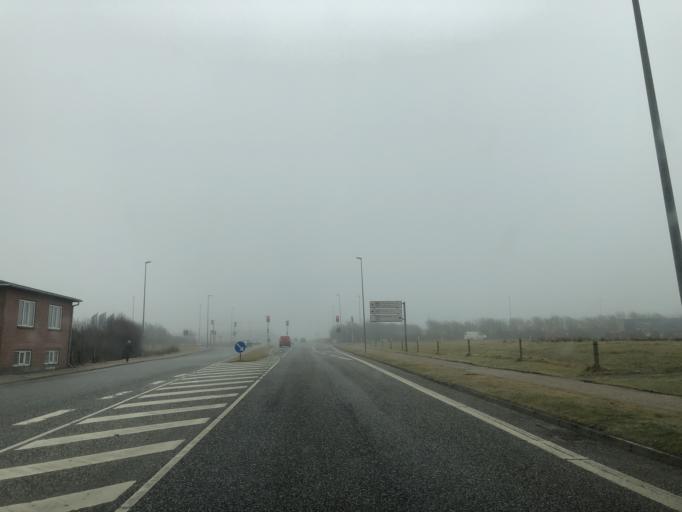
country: DK
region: Central Jutland
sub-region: Lemvig Kommune
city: Lemvig
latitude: 56.5408
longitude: 8.3053
